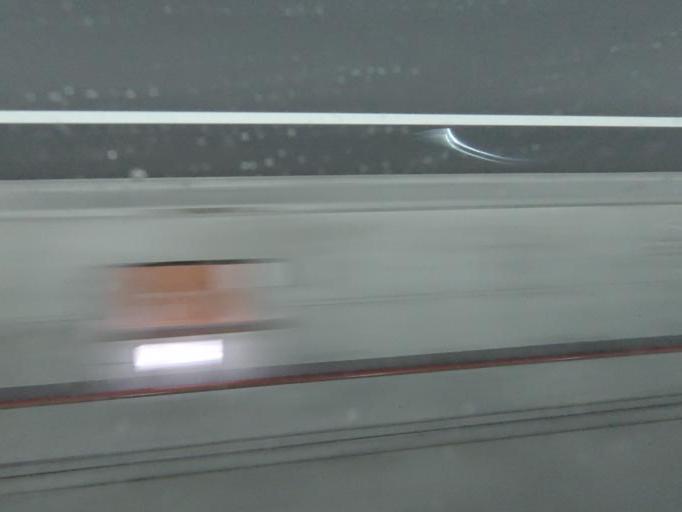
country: PT
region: Vila Real
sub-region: Santa Marta de Penaguiao
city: Santa Marta de Penaguiao
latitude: 41.2800
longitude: -7.8747
